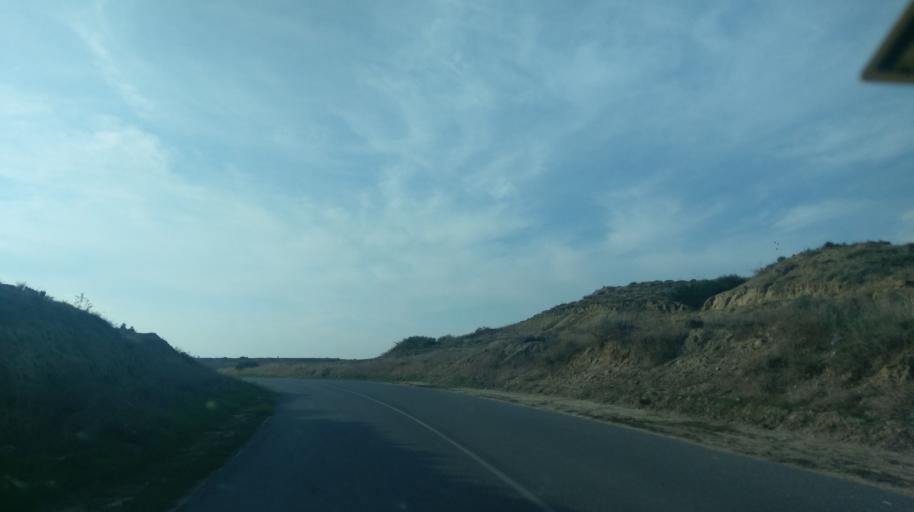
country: CY
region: Ammochostos
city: Achna
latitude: 35.1024
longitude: 33.7798
